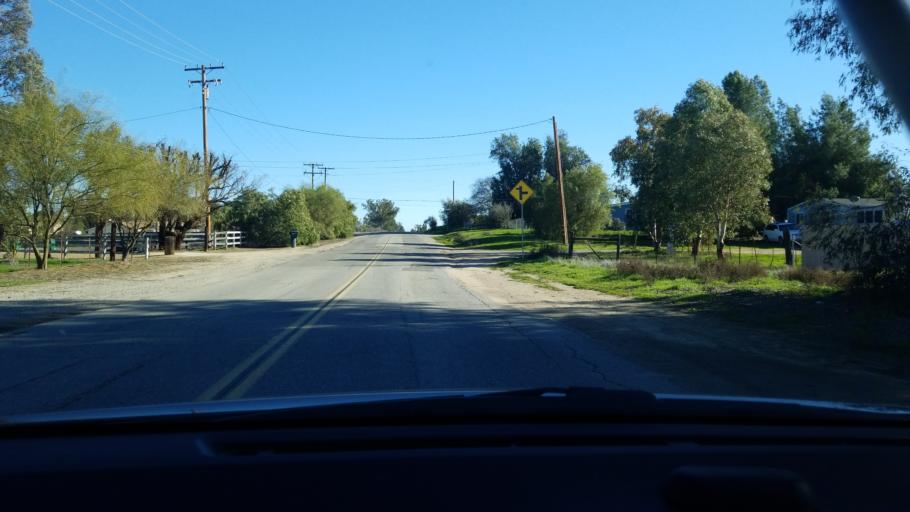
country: US
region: California
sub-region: Riverside County
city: Murrieta
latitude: 33.5491
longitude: -117.2093
